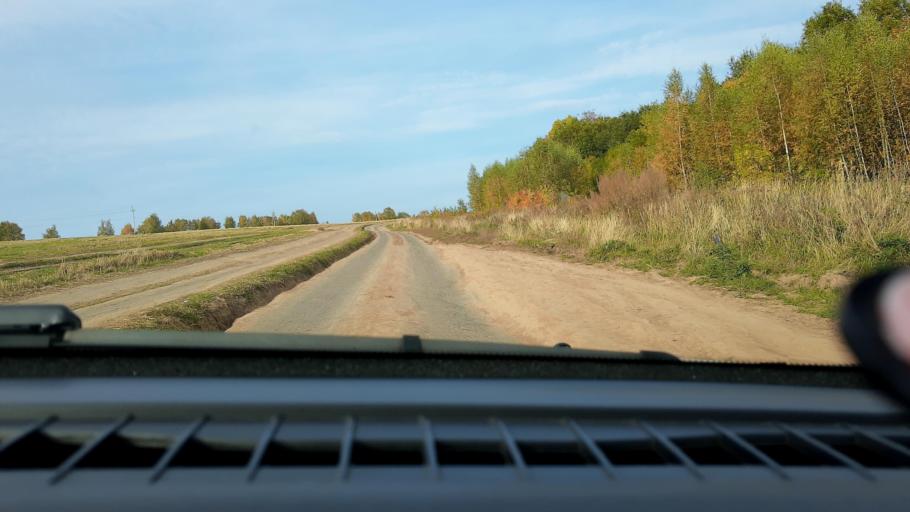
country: RU
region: Nizjnij Novgorod
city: Nizhniy Novgorod
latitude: 56.2008
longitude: 43.9639
